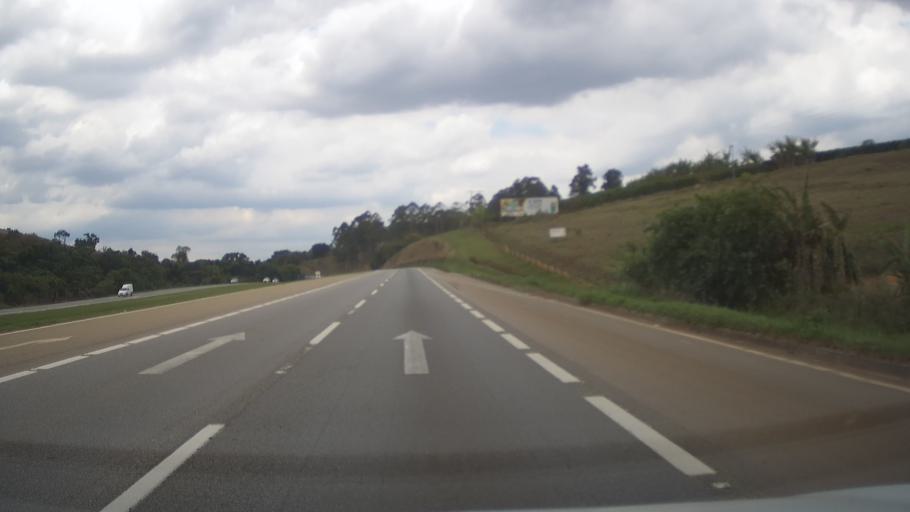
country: BR
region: Minas Gerais
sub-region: Tres Coracoes
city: Tres Coracoes
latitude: -21.5262
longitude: -45.2271
